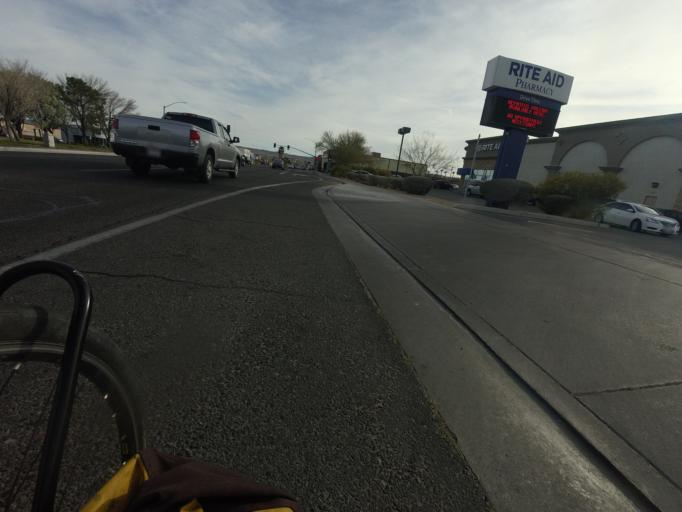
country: US
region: California
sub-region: Kern County
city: Ridgecrest
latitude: 35.6232
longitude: -117.6701
